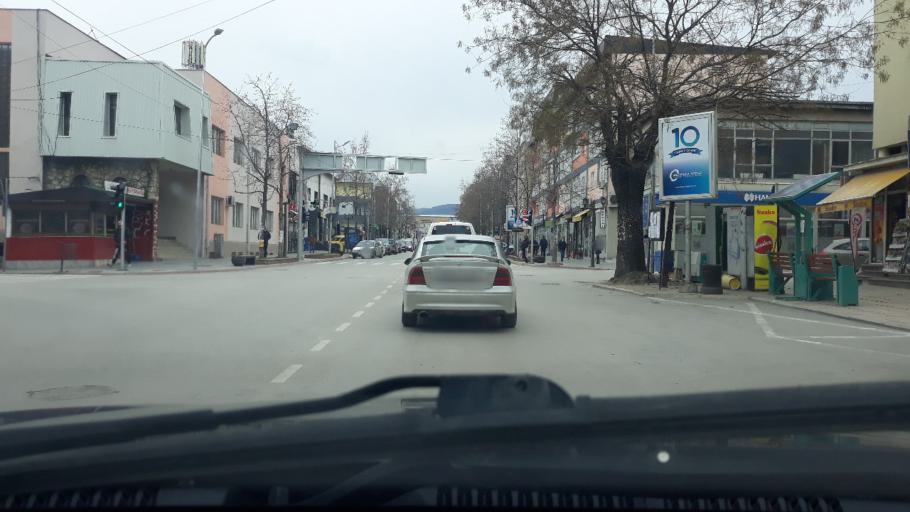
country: MK
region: Kavadarci
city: Kavadarci
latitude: 41.4352
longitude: 22.0114
